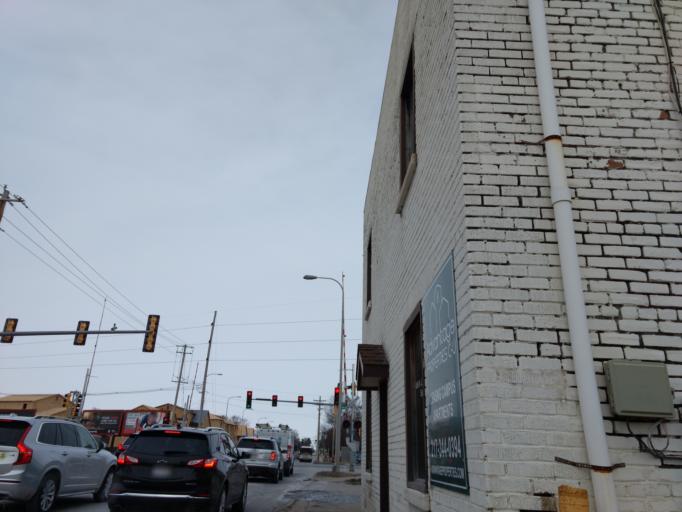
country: US
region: Illinois
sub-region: Champaign County
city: Urbana
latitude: 40.1159
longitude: -88.2192
